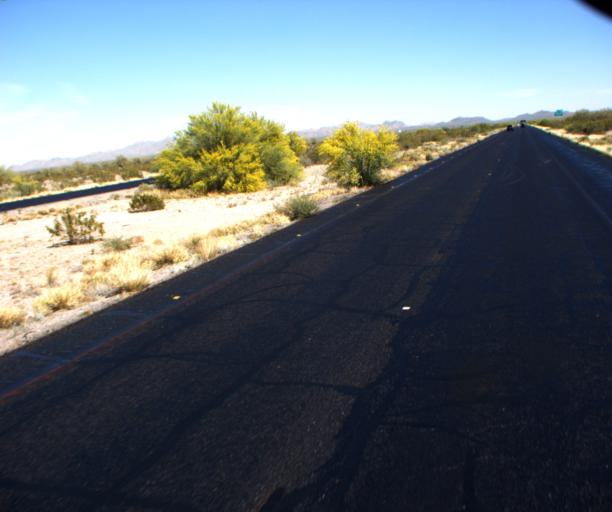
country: US
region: Arizona
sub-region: Pinal County
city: Maricopa
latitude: 32.8451
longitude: -112.2822
